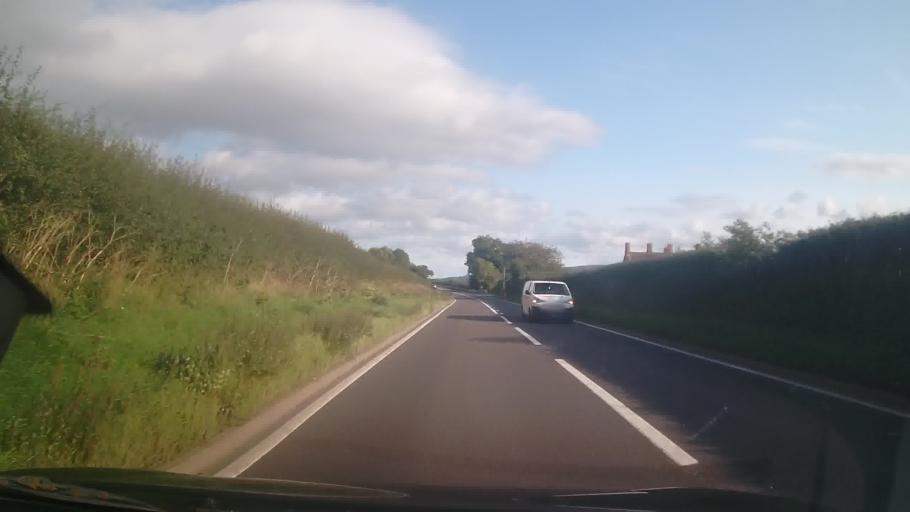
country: GB
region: England
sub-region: Shropshire
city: Bromfield
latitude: 52.3980
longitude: -2.7937
